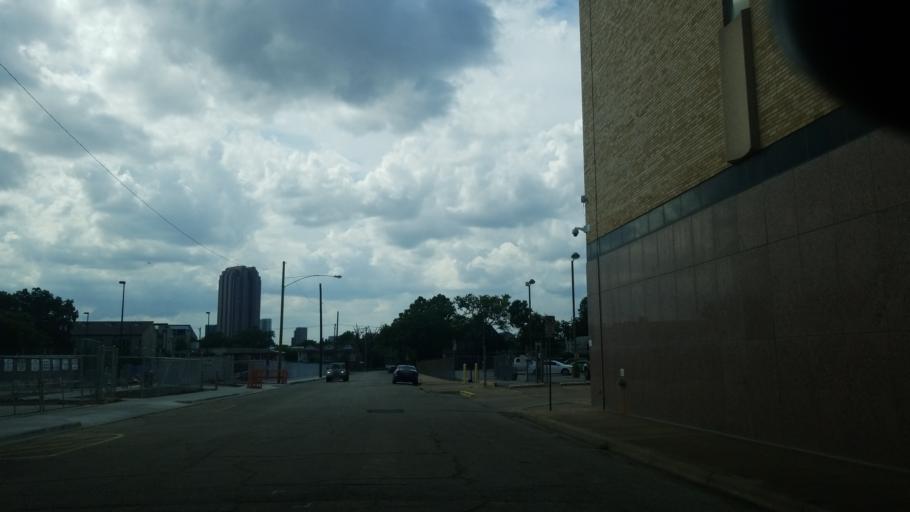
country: US
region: Texas
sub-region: Dallas County
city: Dallas
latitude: 32.7985
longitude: -96.7805
